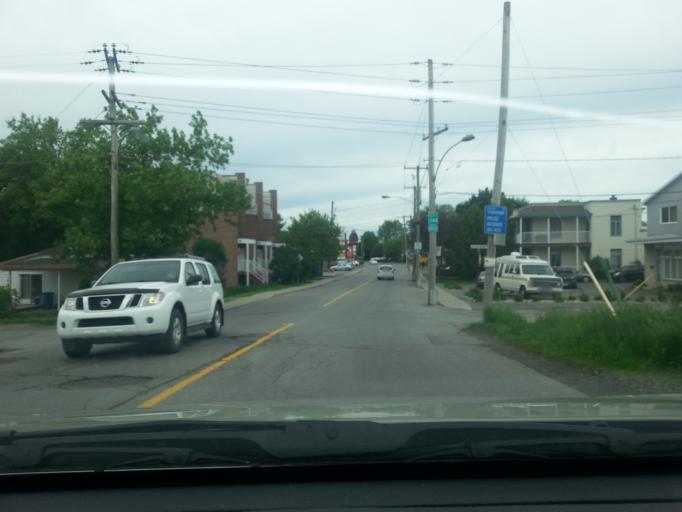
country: CA
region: Quebec
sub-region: Lanaudiere
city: Terrebonne
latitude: 45.6950
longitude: -73.6216
